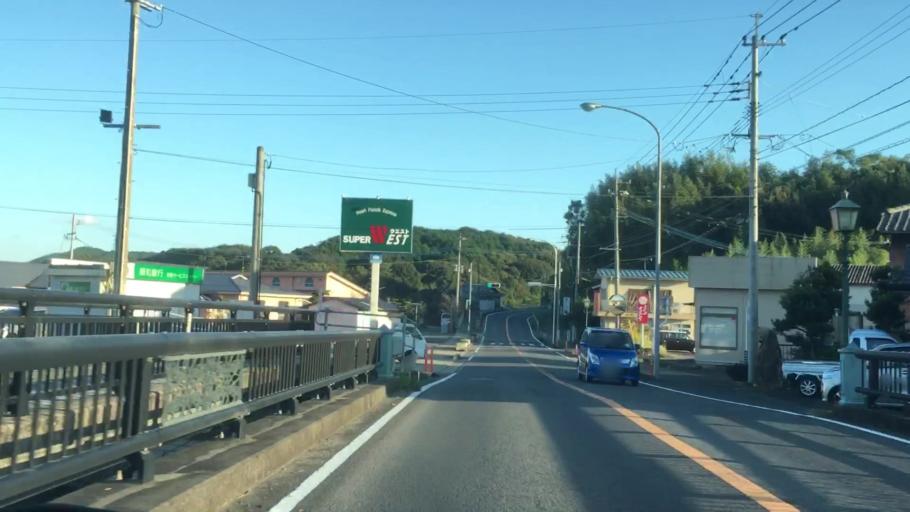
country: JP
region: Nagasaki
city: Sasebo
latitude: 33.0011
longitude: 129.7309
